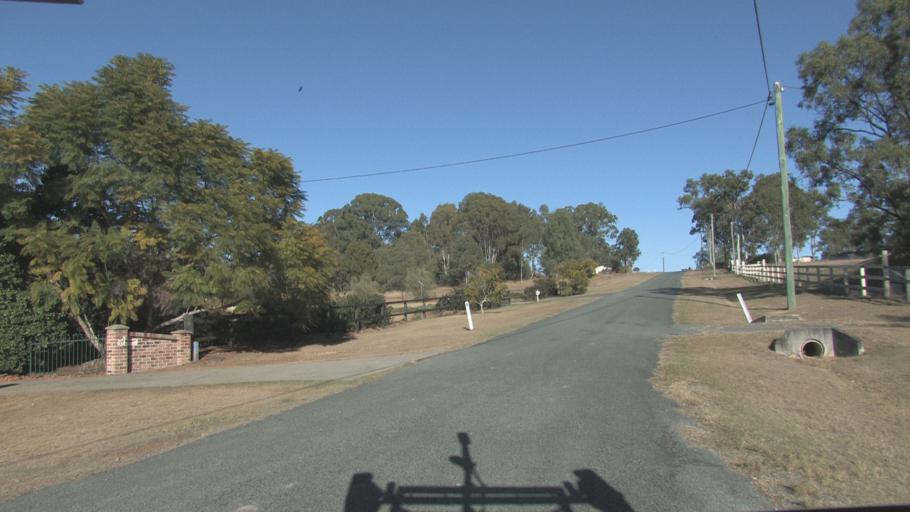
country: AU
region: Queensland
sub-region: Logan
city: Cedar Vale
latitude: -27.8349
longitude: 153.0107
